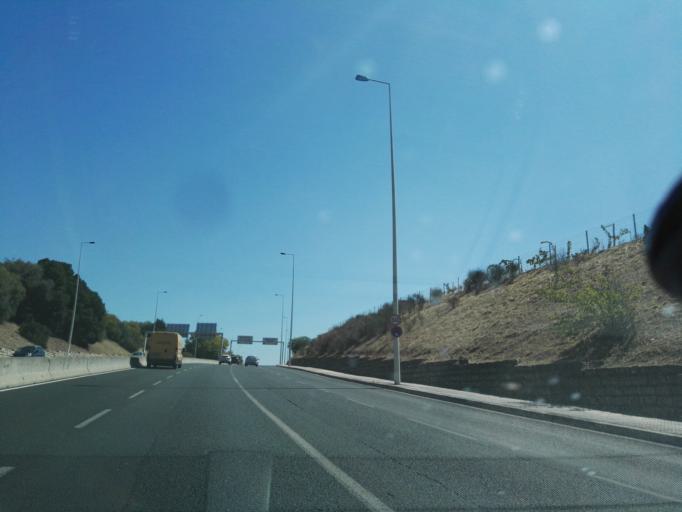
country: PT
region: Lisbon
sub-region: Loures
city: Moscavide
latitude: 38.7629
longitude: -9.1271
